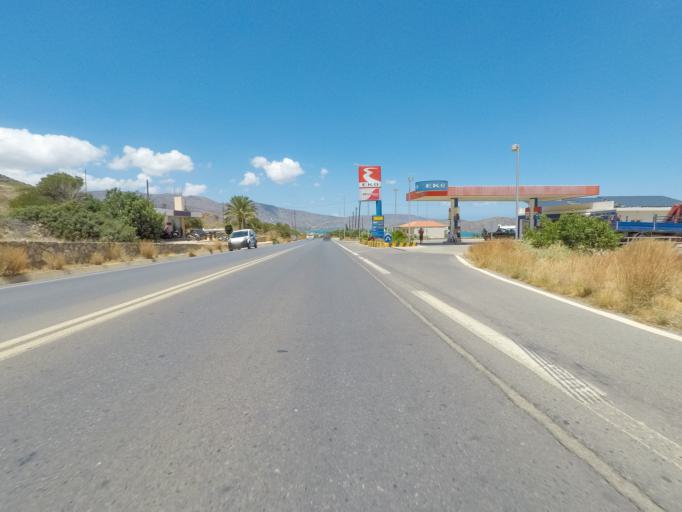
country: GR
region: Crete
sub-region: Nomos Lasithiou
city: Skhisma
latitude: 35.2429
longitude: 25.7258
